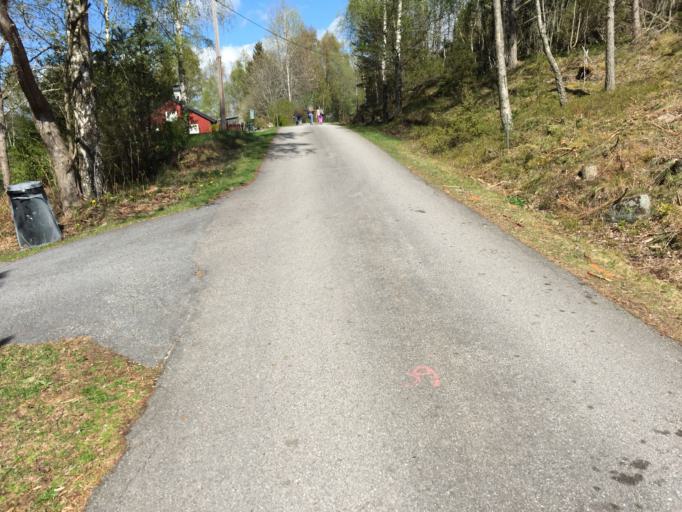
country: SE
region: Vaestra Goetaland
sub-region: Stromstads Kommun
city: Stroemstad
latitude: 58.9902
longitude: 11.1725
